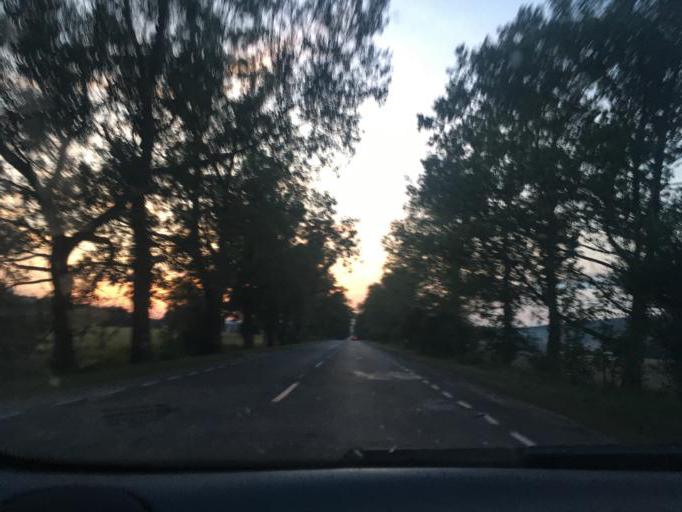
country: PL
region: Lower Silesian Voivodeship
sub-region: Powiat walbrzyski
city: Czarny Bor
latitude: 50.7732
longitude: 16.1220
